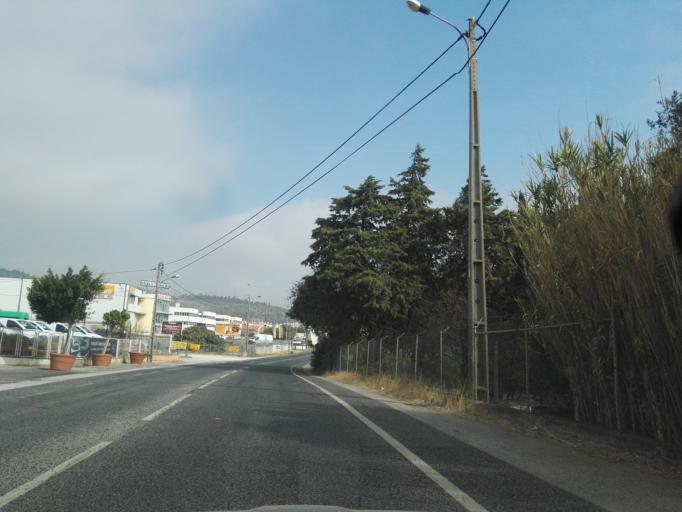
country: PT
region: Lisbon
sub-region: Vila Franca de Xira
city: Sobralinho
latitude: 38.9100
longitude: -9.0263
